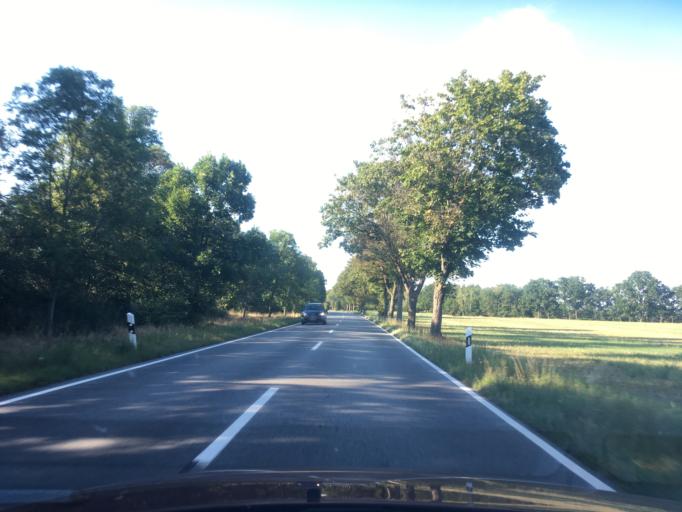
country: PL
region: Lower Silesian Voivodeship
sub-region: Powiat zgorzelecki
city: Piensk
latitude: 51.2703
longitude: 15.0291
